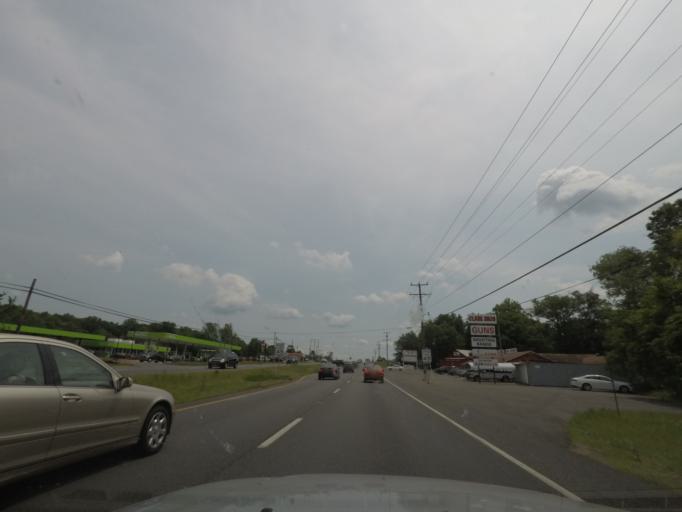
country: US
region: Virginia
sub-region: Fauquier County
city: Bealeton
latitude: 38.6253
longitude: -77.8008
